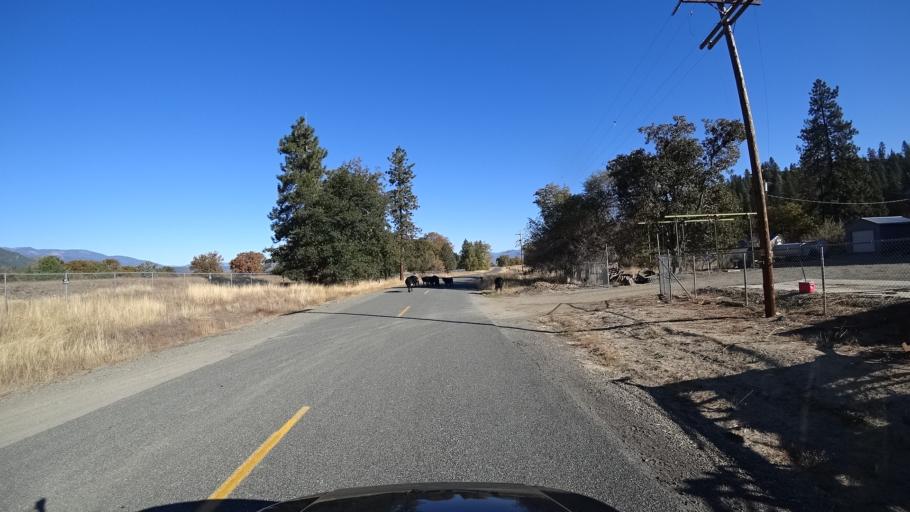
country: US
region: California
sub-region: Siskiyou County
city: Yreka
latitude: 41.4656
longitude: -122.8837
